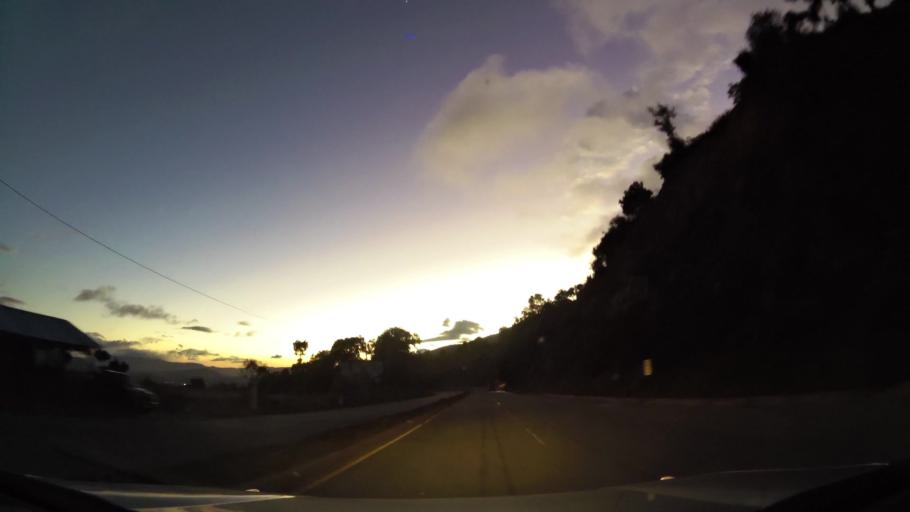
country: GT
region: Chimaltenango
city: Santa Apolonia
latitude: 14.7921
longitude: -90.9782
